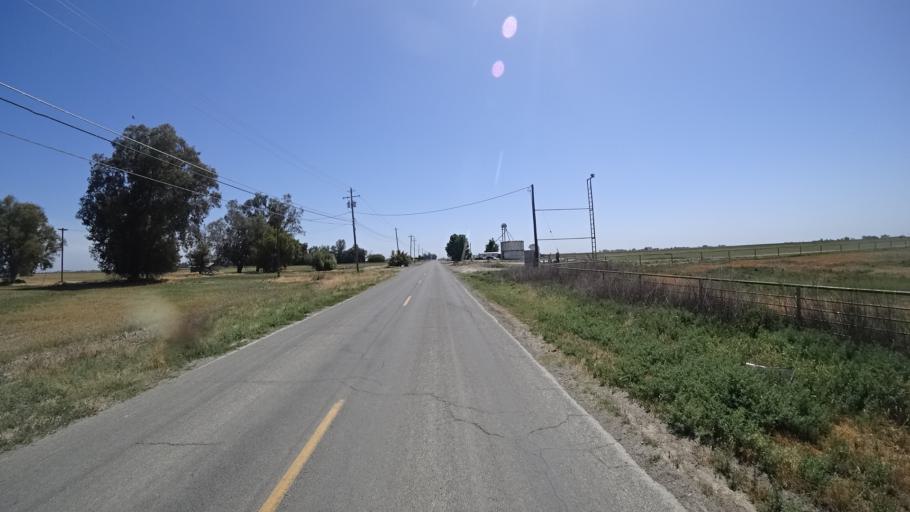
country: US
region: California
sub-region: Kings County
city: Stratford
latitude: 36.1894
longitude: -119.8122
